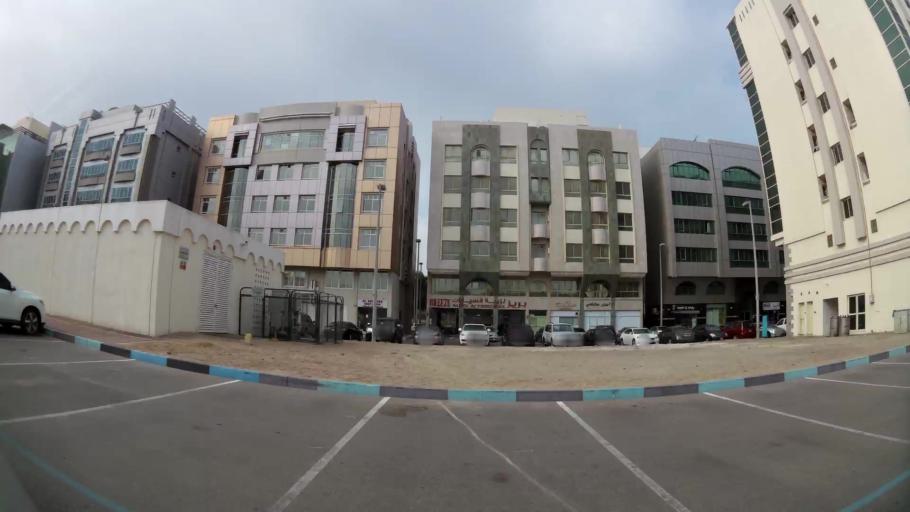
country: AE
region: Abu Dhabi
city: Abu Dhabi
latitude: 24.4689
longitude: 54.3819
